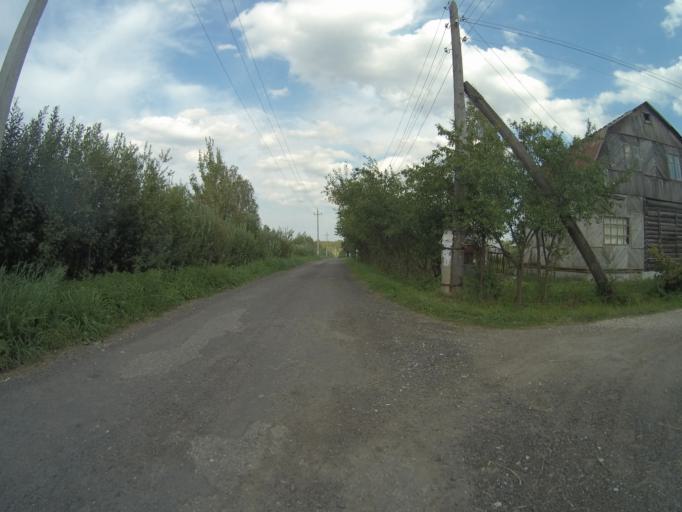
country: RU
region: Vladimir
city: Bogolyubovo
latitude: 56.1061
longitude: 40.5613
